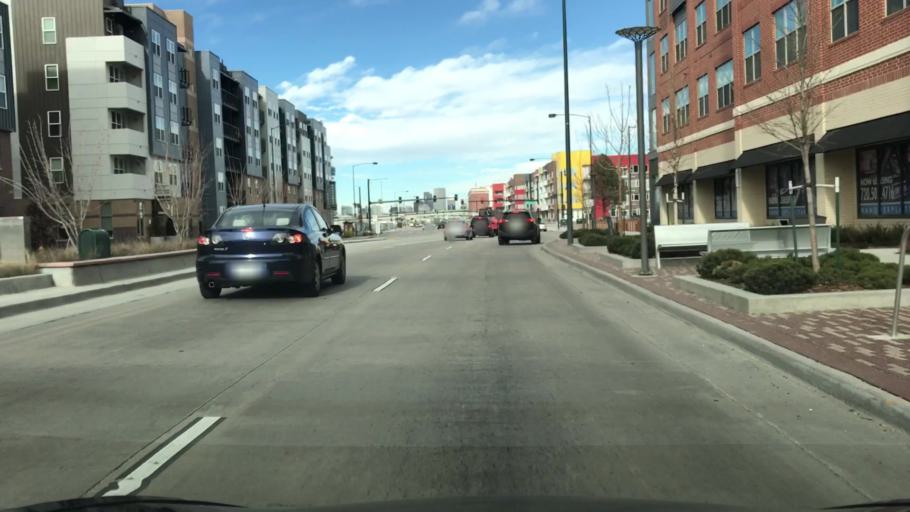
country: US
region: Colorado
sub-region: Denver County
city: Denver
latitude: 39.6949
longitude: -104.9874
